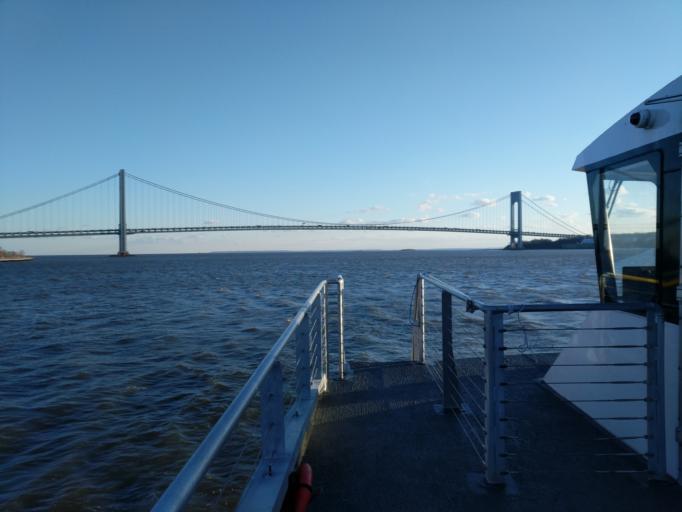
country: US
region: New York
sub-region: Kings County
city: Bensonhurst
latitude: 40.6202
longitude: -74.0439
